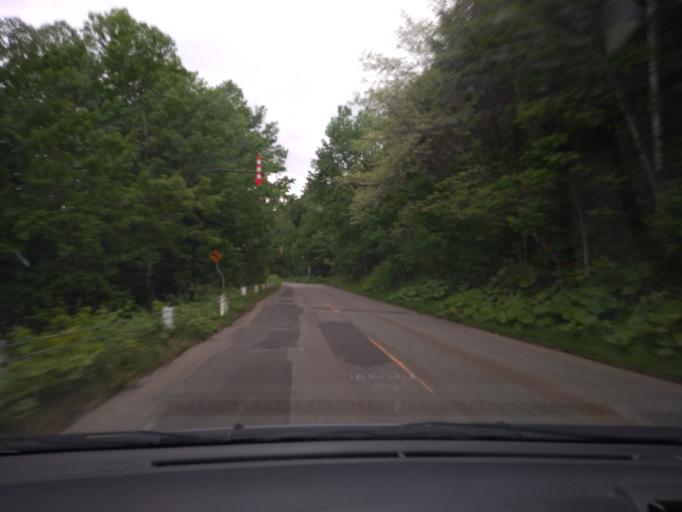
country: JP
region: Hokkaido
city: Shimo-furano
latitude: 43.1379
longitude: 142.4733
